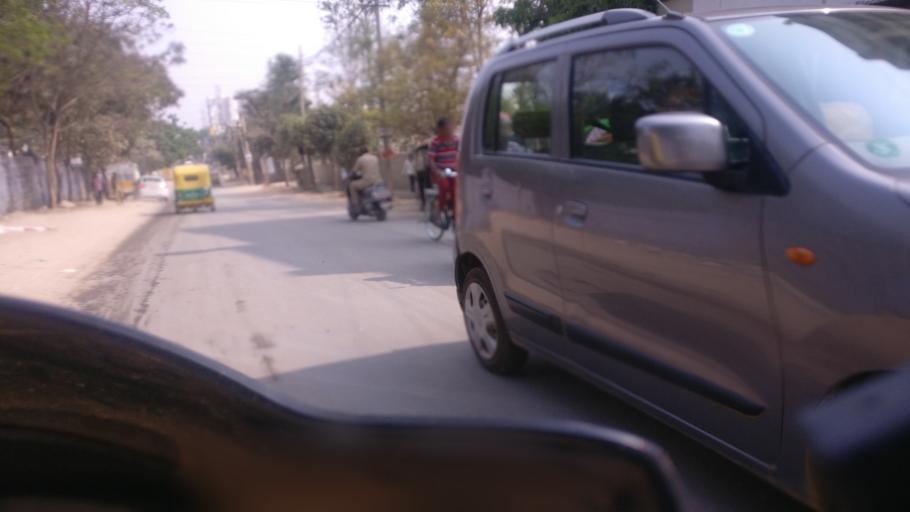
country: IN
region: Karnataka
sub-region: Bangalore Urban
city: Bangalore
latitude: 12.8862
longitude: 77.6725
